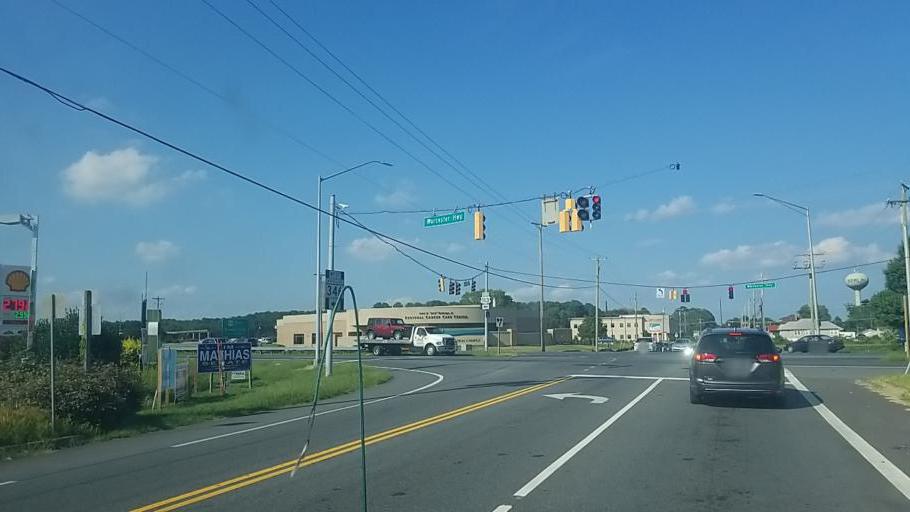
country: US
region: Maryland
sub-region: Worcester County
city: Berlin
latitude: 38.3349
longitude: -75.2114
